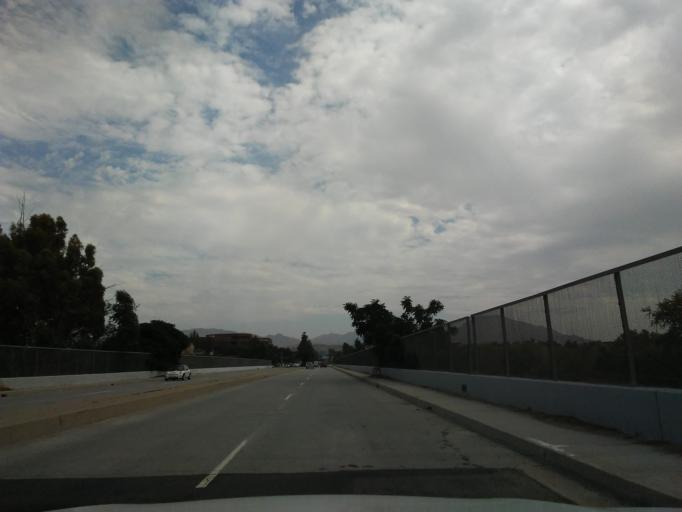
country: US
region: California
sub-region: San Bernardino County
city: Loma Linda
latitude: 34.0721
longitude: -117.2789
